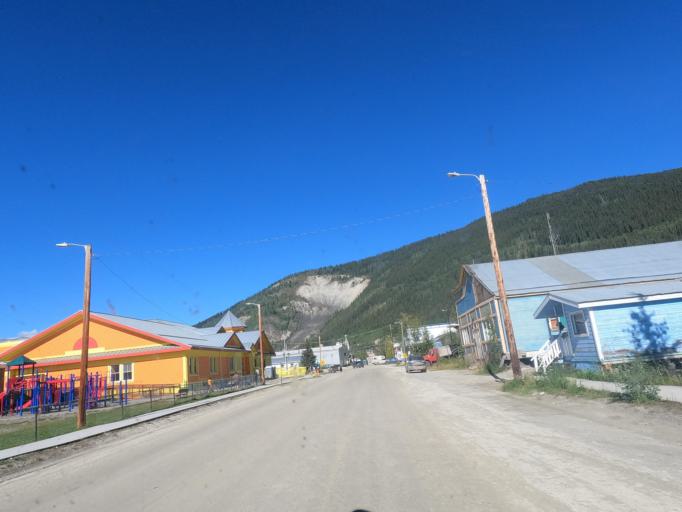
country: CA
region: Yukon
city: Dawson City
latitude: 64.0599
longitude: -139.4311
